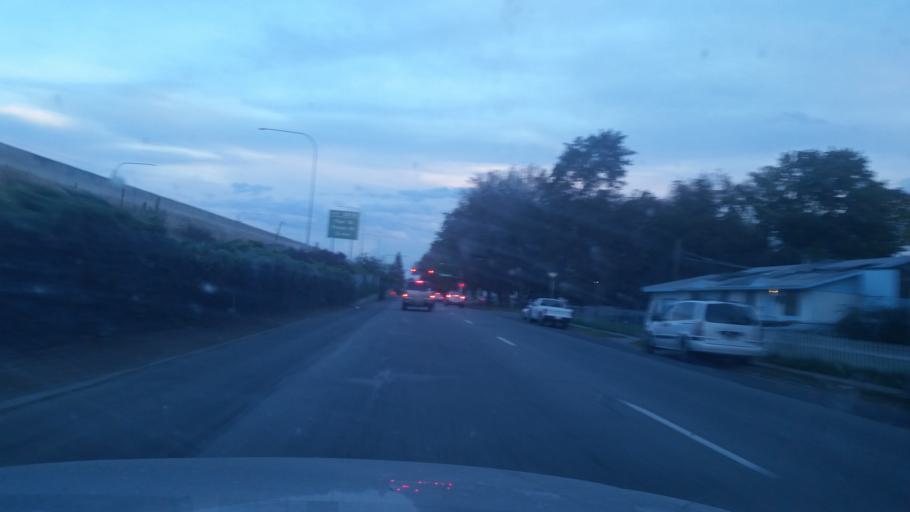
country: US
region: Washington
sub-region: Spokane County
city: Spokane
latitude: 47.6537
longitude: -117.3777
